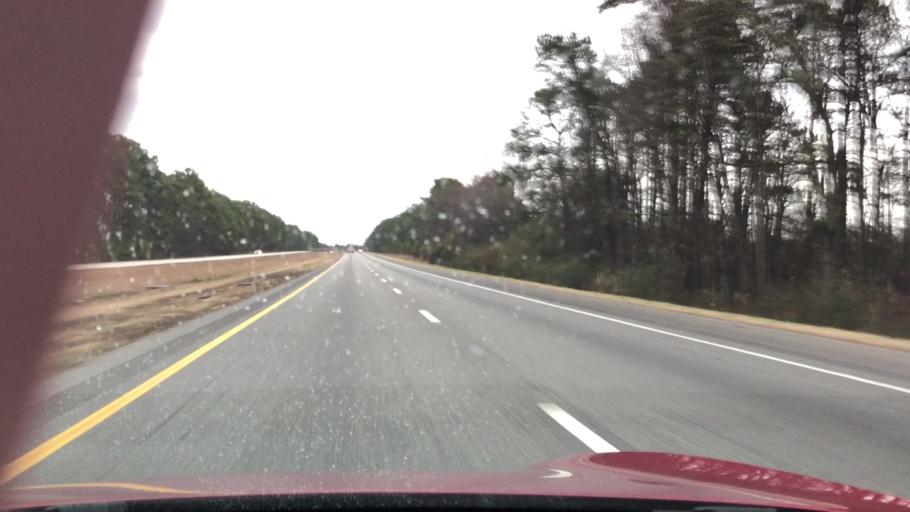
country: US
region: South Carolina
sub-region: Dillon County
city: Latta
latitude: 34.3899
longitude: -79.4622
